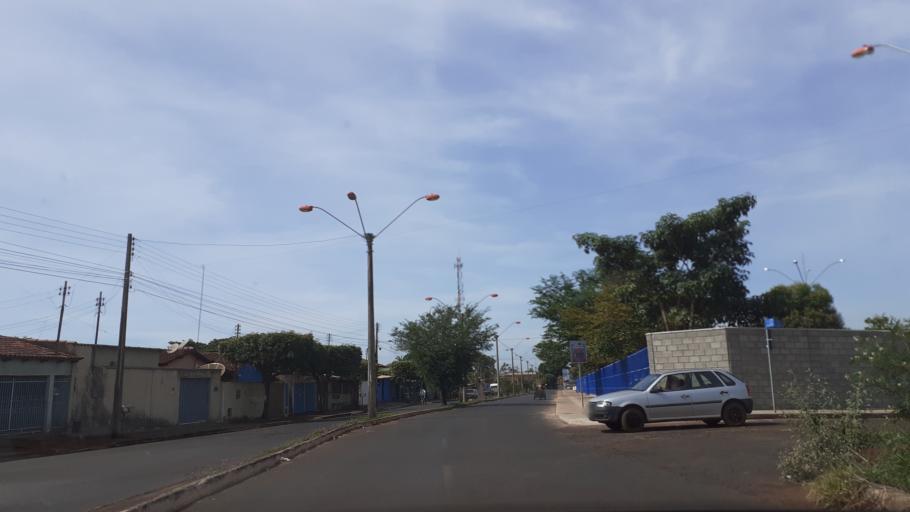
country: BR
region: Goias
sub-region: Itumbiara
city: Itumbiara
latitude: -18.4172
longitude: -49.2348
